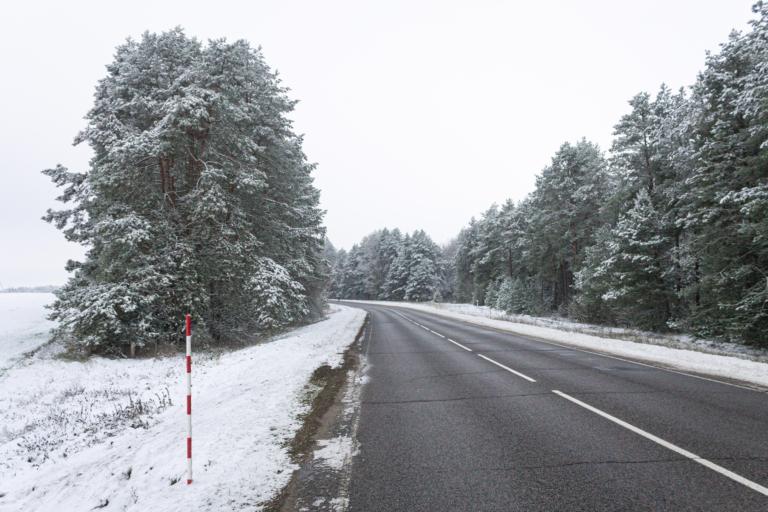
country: BY
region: Brest
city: Kamyanyets
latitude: 52.3836
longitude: 23.8596
